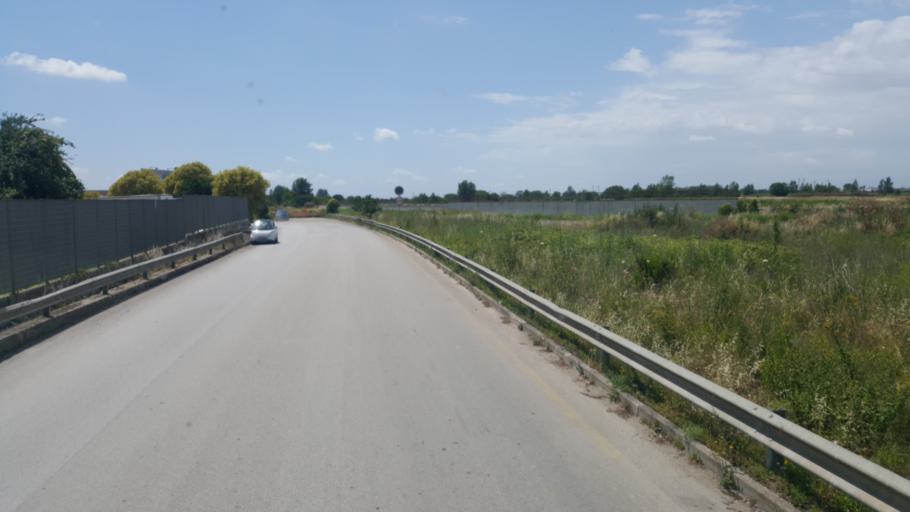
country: IT
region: Campania
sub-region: Provincia di Caserta
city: Maddaloni
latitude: 41.0119
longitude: 14.3704
